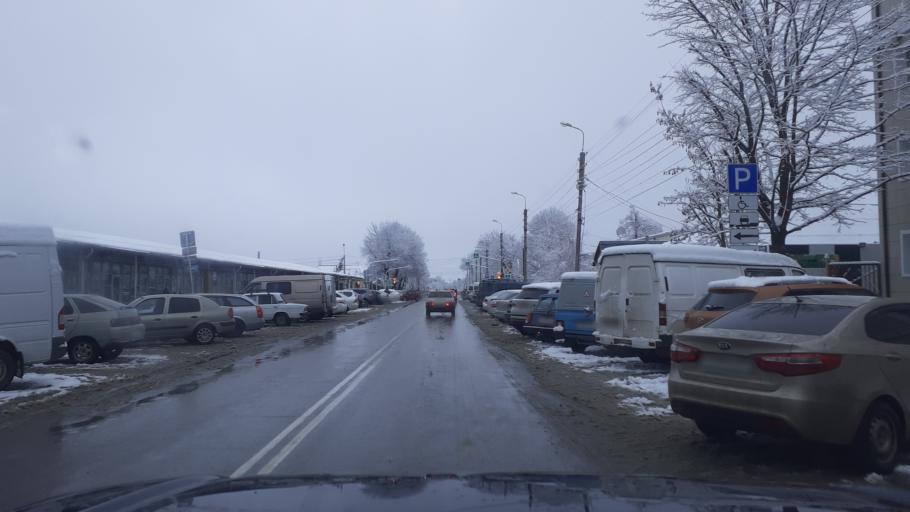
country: RU
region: Adygeya
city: Maykop
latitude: 44.6091
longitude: 40.1121
